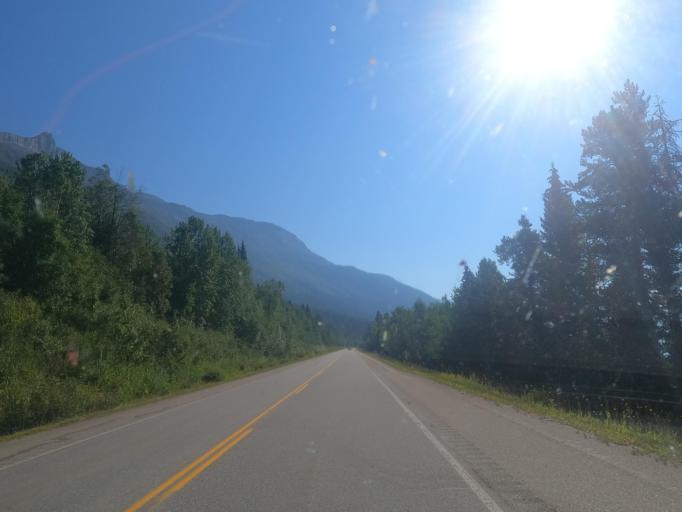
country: CA
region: Alberta
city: Jasper Park Lodge
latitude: 52.9728
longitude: -118.9504
